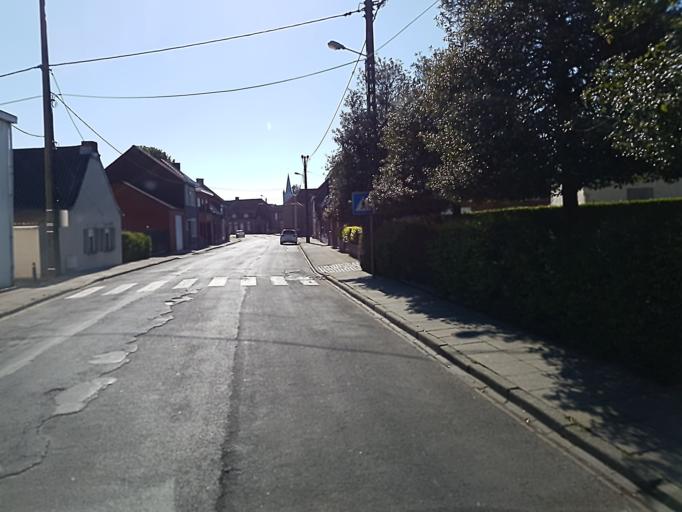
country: BE
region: Wallonia
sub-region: Province du Hainaut
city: Estaimpuis
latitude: 50.7316
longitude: 3.2974
